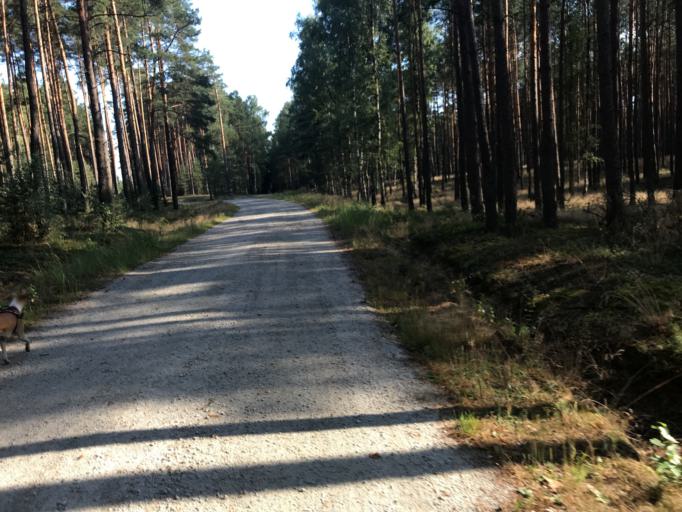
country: PL
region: Greater Poland Voivodeship
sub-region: Powiat szamotulski
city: Obrzycko
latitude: 52.7354
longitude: 16.5579
